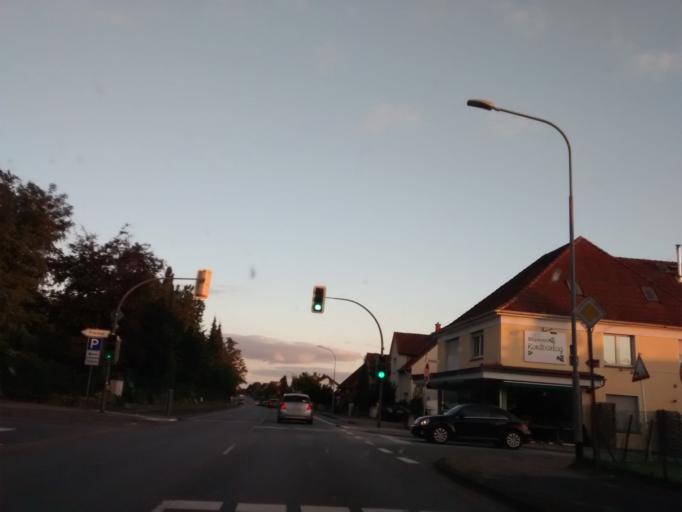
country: DE
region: North Rhine-Westphalia
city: Halle
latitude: 52.0561
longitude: 8.3698
